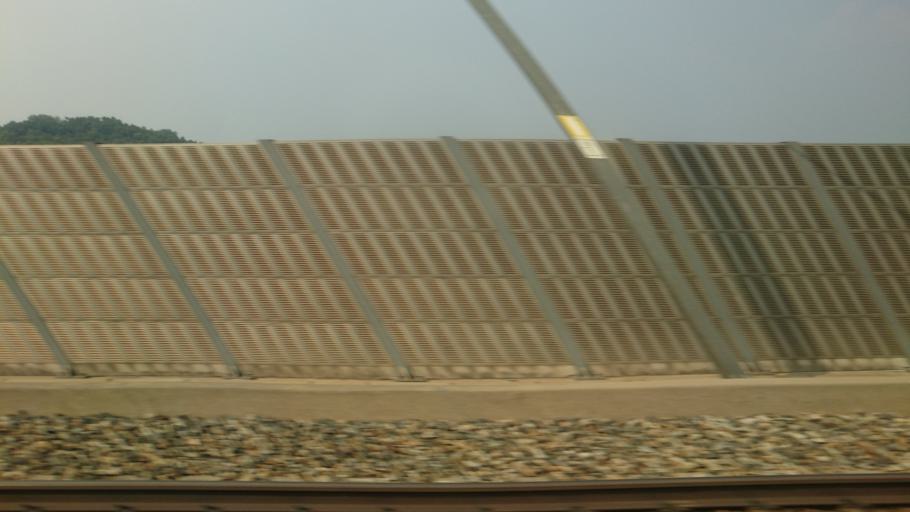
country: KR
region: Chungcheongnam-do
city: Cheonan
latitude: 36.7250
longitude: 127.1576
